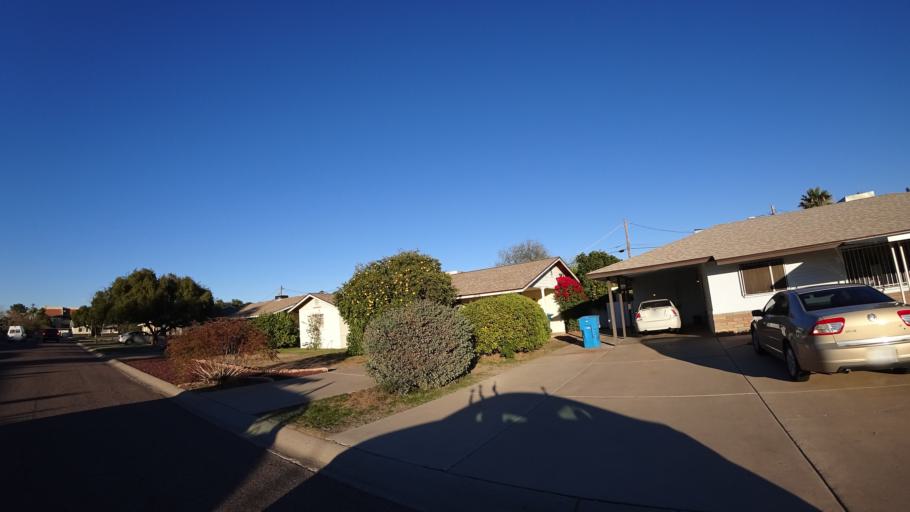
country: US
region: Arizona
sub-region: Maricopa County
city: Phoenix
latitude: 33.4856
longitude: -112.0381
